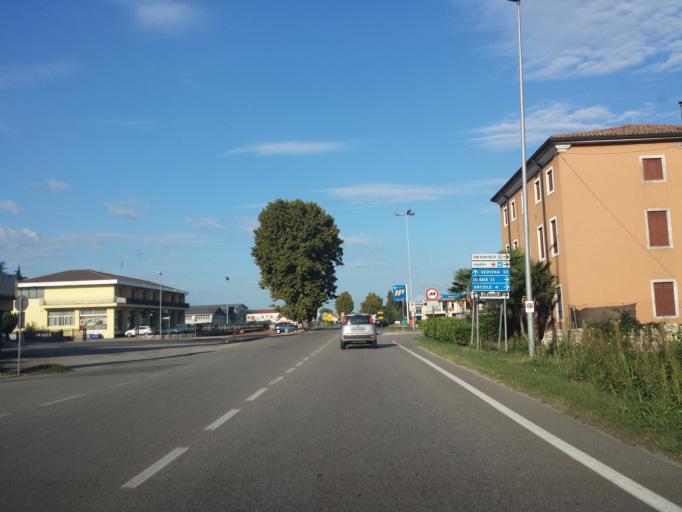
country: IT
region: Veneto
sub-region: Provincia di Verona
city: San Bonifacio
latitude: 45.4049
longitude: 11.2781
